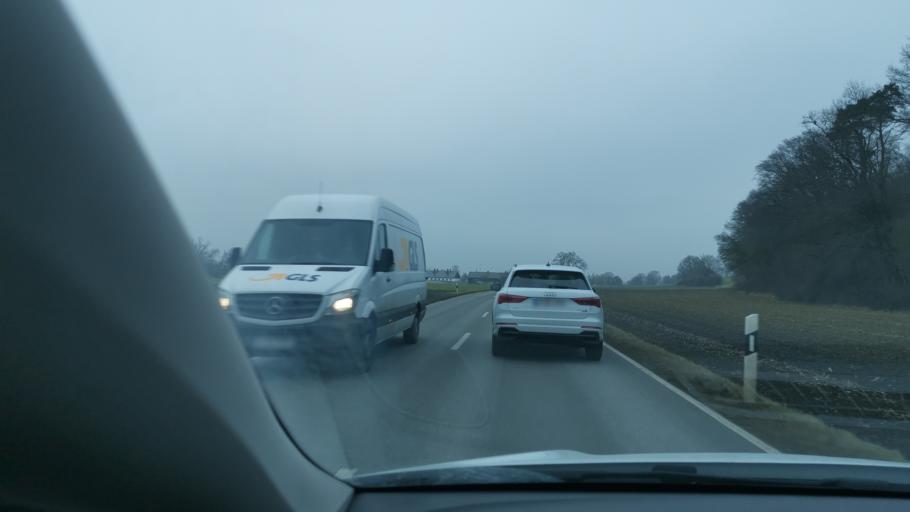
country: DE
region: Bavaria
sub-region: Swabia
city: Thierhaupten
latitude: 48.5473
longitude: 10.9117
